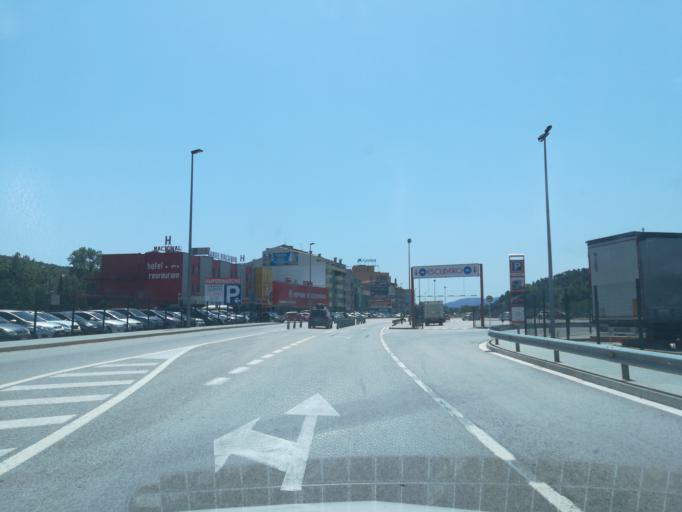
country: ES
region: Catalonia
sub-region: Provincia de Girona
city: la Jonquera
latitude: 42.4228
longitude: 2.8701
